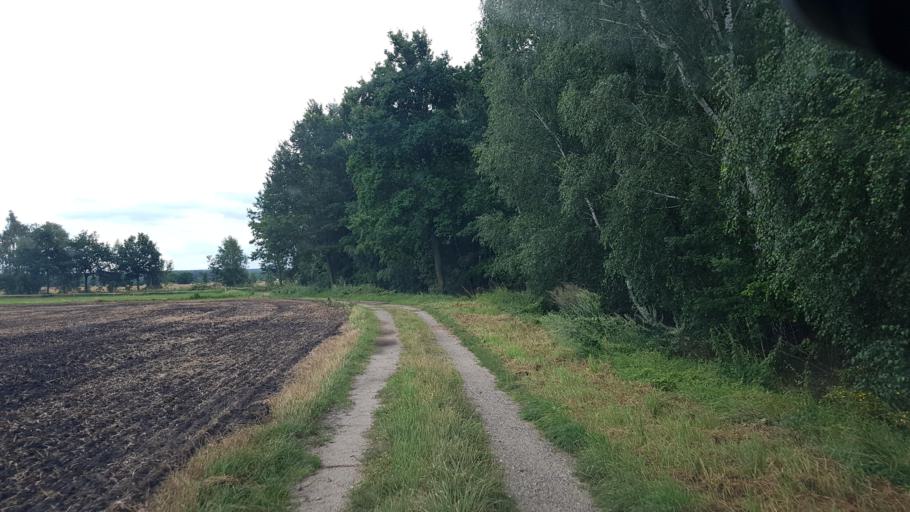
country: DE
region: Brandenburg
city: Schilda
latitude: 51.6466
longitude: 13.3946
